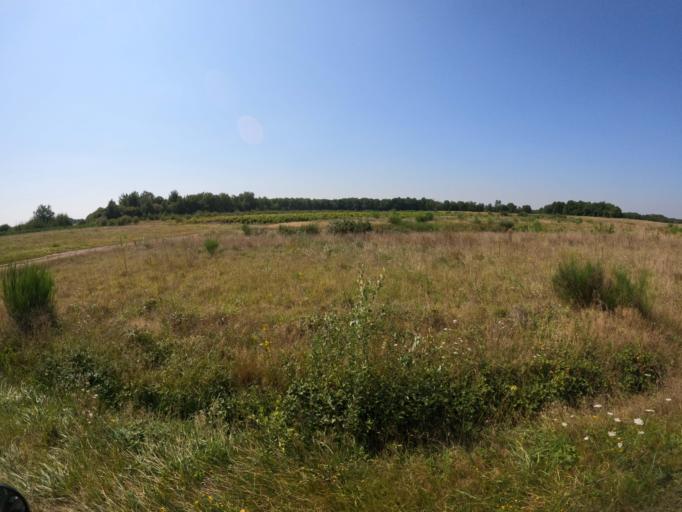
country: FR
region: Pays de la Loire
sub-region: Departement de la Loire-Atlantique
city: Pont-Saint-Martin
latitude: 47.1179
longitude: -1.5500
